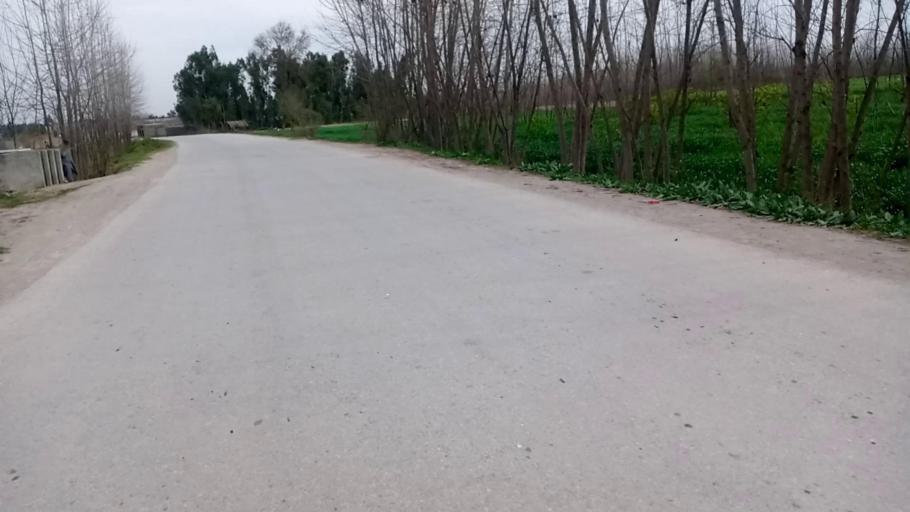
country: PK
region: Khyber Pakhtunkhwa
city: Charsadda
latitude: 34.0619
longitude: 71.6981
